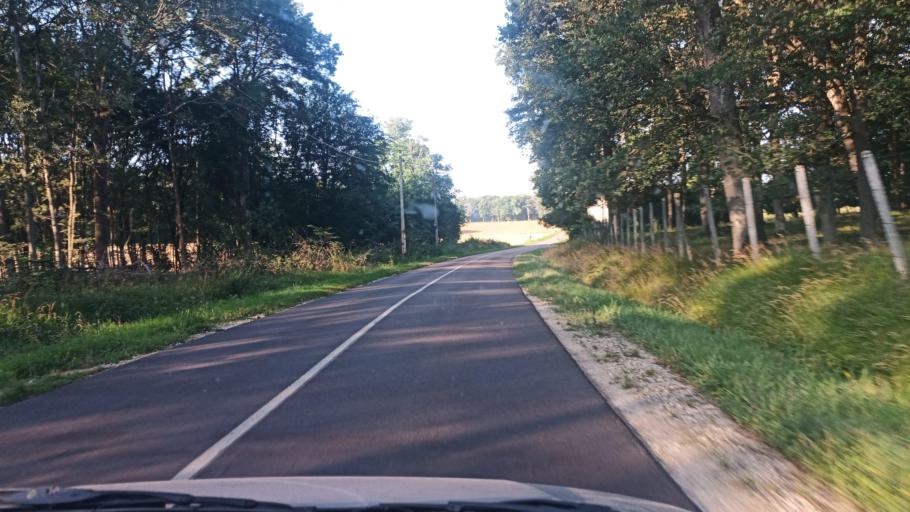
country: FR
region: Bourgogne
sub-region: Departement de l'Yonne
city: Pont-sur-Yonne
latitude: 48.2551
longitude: 3.1696
